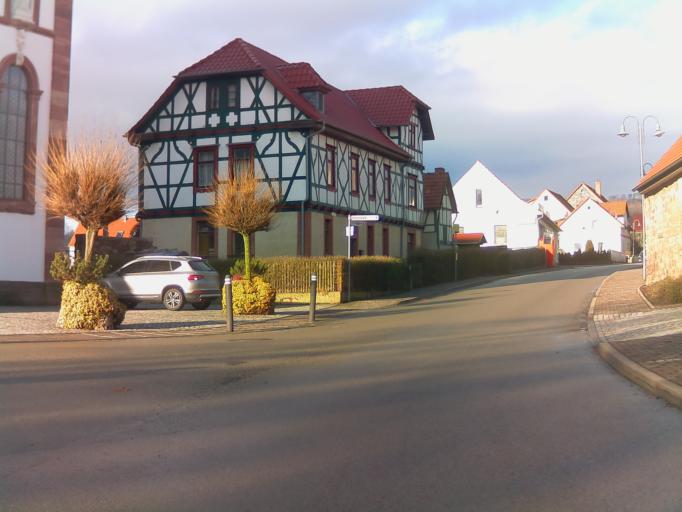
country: DE
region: Thuringia
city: Dermbach
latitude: 50.7174
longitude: 10.1167
